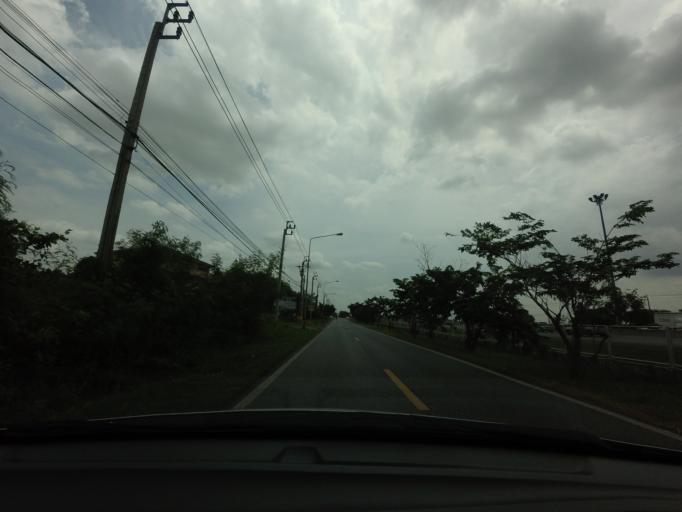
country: TH
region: Bangkok
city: Khan Na Yao
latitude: 13.8783
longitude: 100.6838
